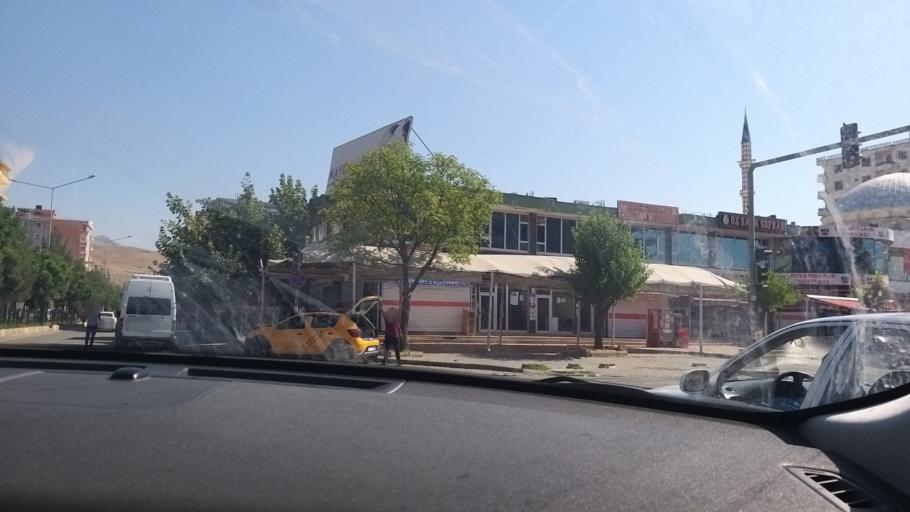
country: TR
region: Batman
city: Kozluk
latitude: 38.1663
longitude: 41.5011
